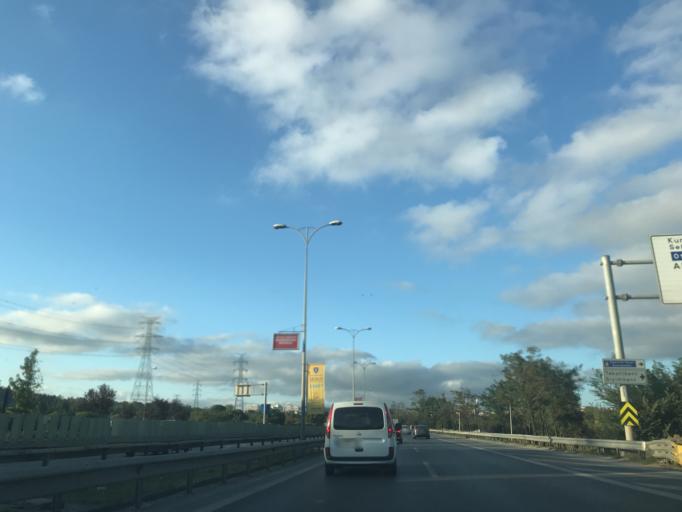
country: TR
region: Istanbul
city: Esenler
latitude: 41.0572
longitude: 28.8861
